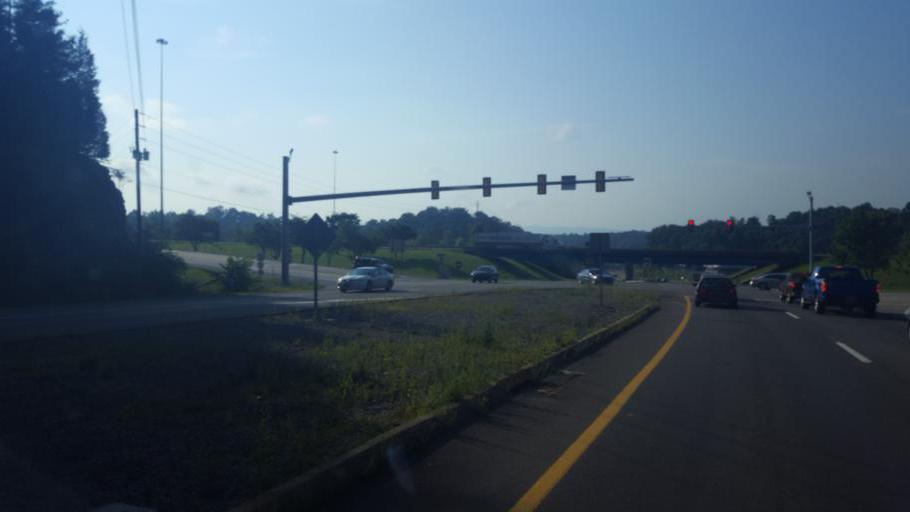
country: US
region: Tennessee
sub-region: Sullivan County
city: Blountville
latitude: 36.5455
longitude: -82.3369
